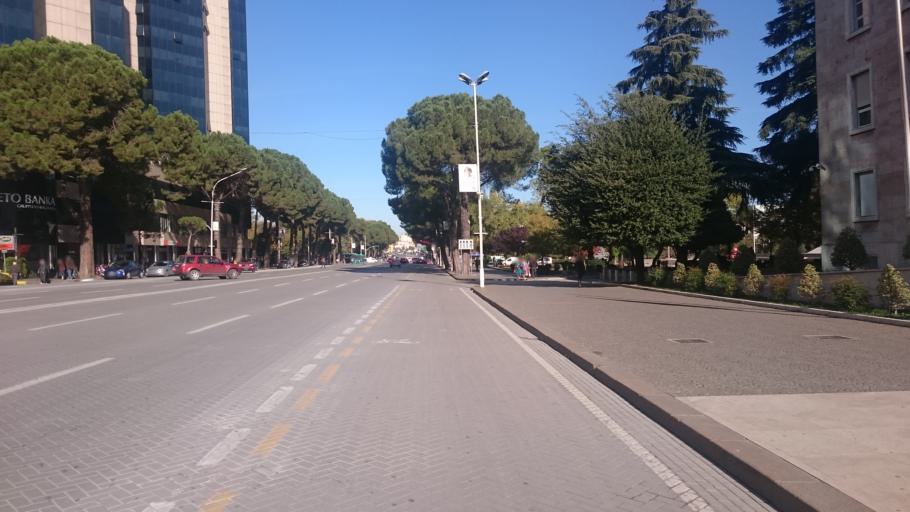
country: AL
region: Tirane
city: Tirana
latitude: 41.3217
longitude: 19.8204
